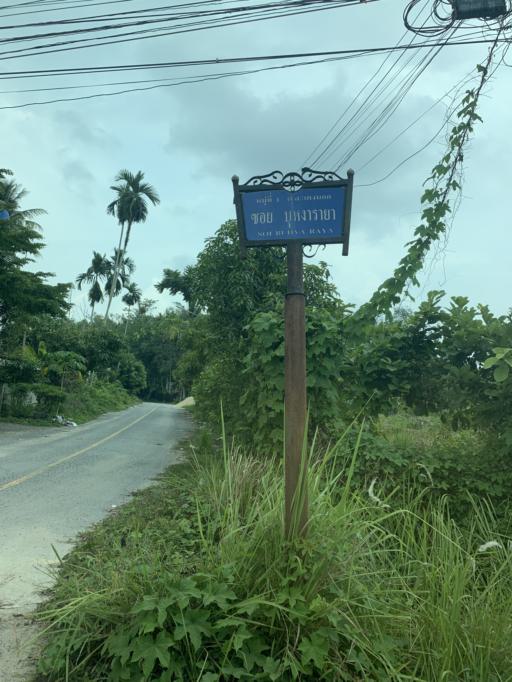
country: TH
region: Yala
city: Yala
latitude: 6.5242
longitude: 101.2893
